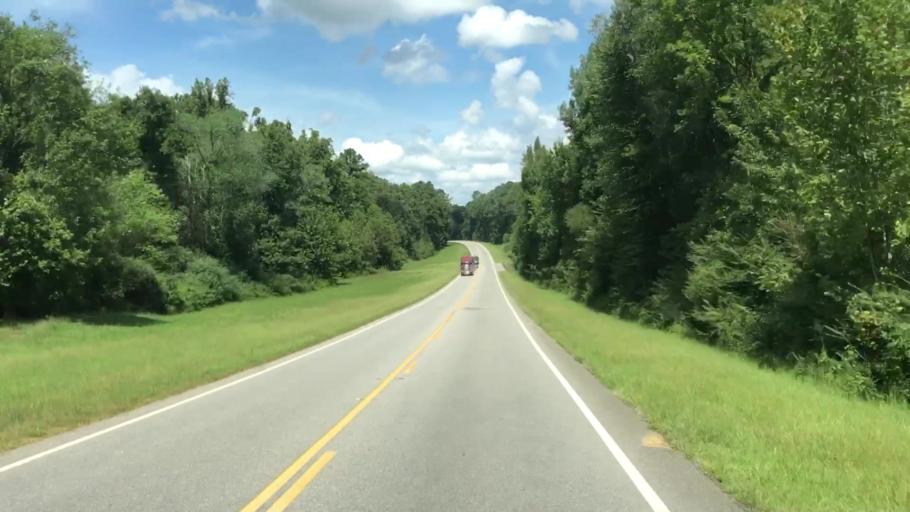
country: US
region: Georgia
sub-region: Greene County
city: Greensboro
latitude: 33.6905
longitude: -83.2755
